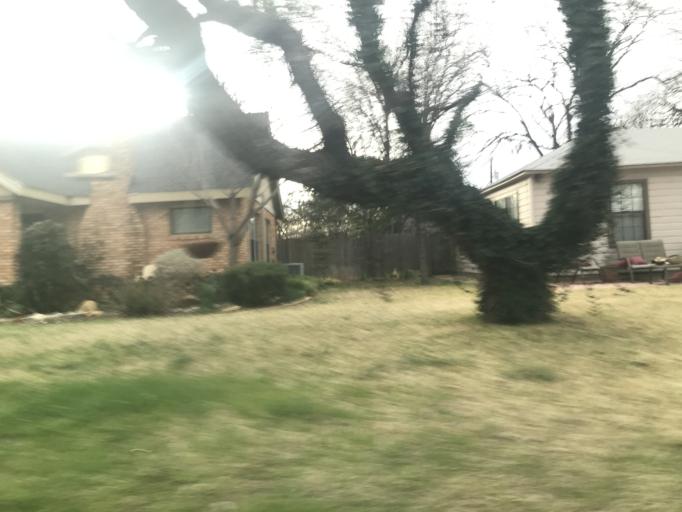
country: US
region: Texas
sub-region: Taylor County
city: Abilene
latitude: 32.4408
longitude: -99.7657
